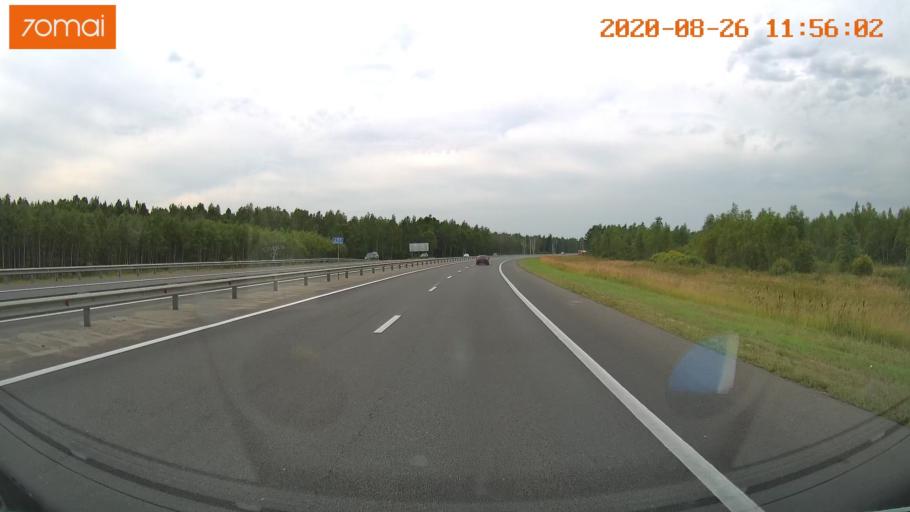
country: RU
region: Rjazan
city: Kiritsy
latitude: 54.2655
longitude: 40.3869
